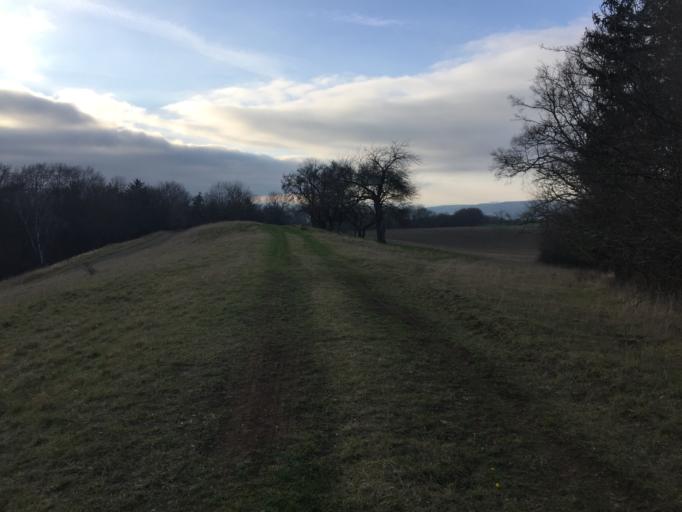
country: DE
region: Thuringia
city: Ranis
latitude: 50.6719
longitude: 11.5764
